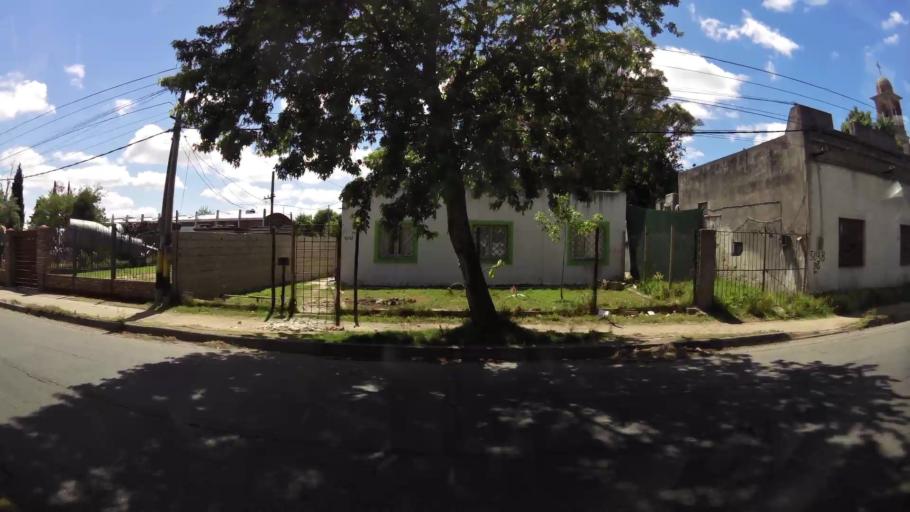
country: UY
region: Montevideo
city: Montevideo
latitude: -34.8518
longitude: -56.1329
